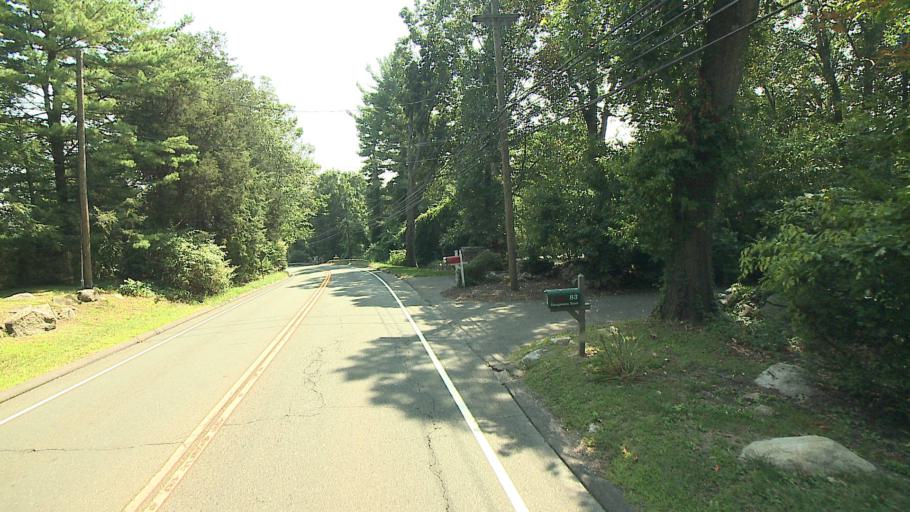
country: US
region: Connecticut
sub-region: Fairfield County
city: Georgetown
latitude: 41.2481
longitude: -73.4168
